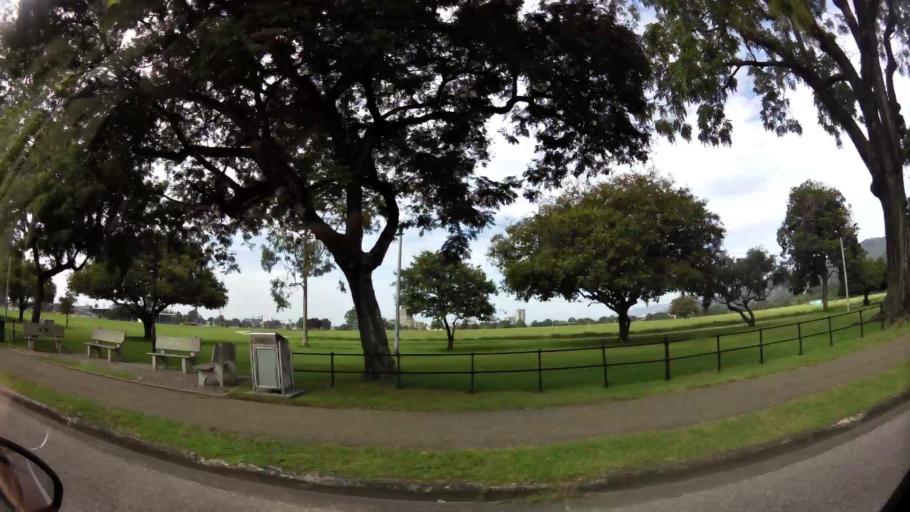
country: TT
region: City of Port of Spain
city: Port-of-Spain
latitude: 10.6694
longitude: -61.5098
